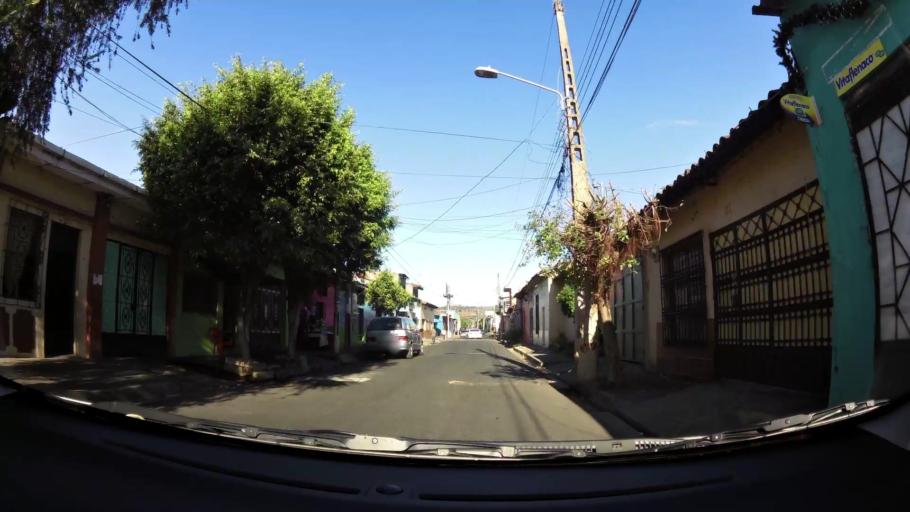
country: SV
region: Sonsonate
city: Sonsonate
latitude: 13.7183
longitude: -89.7210
